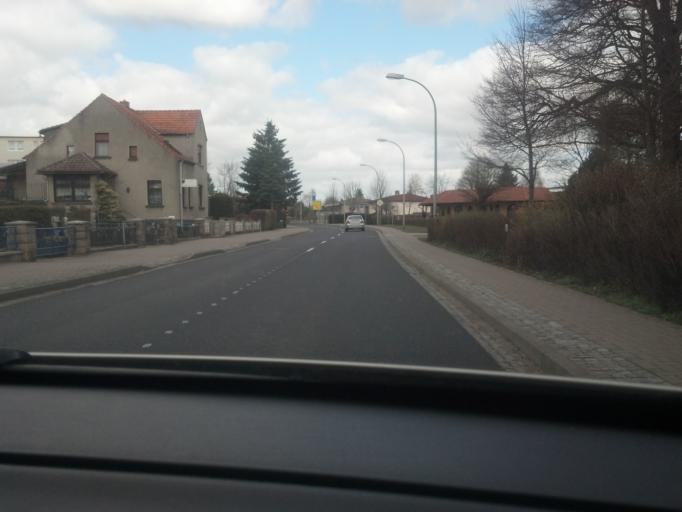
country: DE
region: Brandenburg
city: Gerdshagen
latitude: 53.3175
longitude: 12.2409
